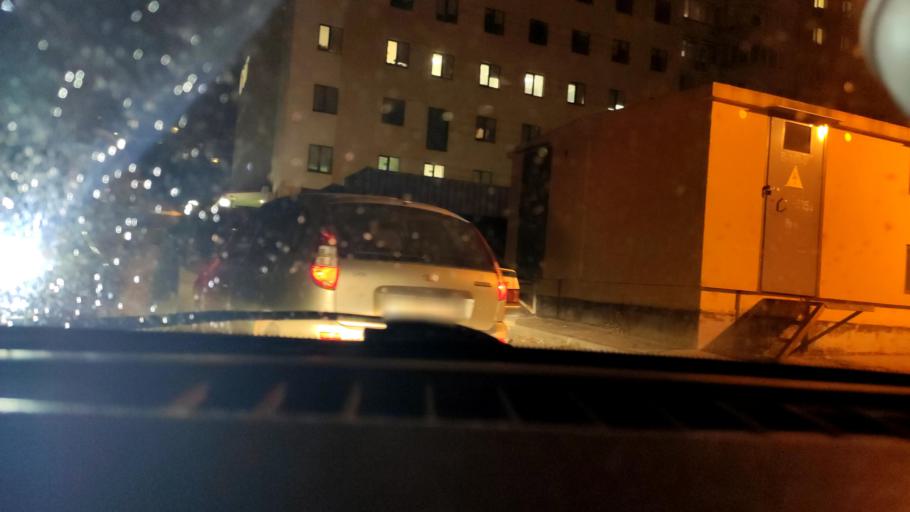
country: RU
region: Samara
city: Samara
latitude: 53.2477
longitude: 50.2371
